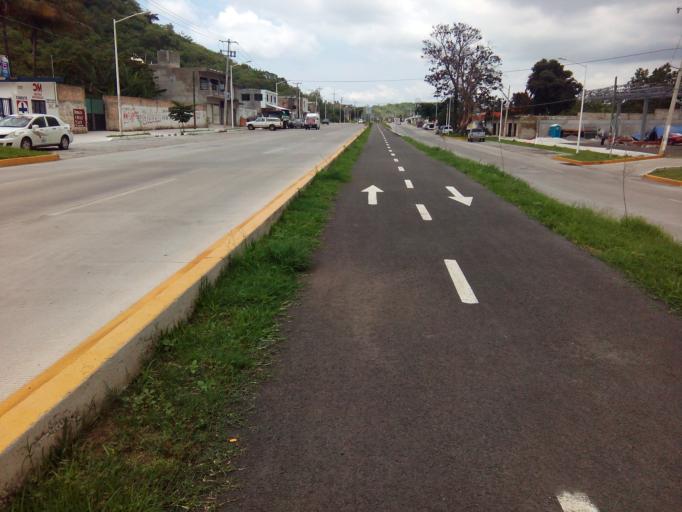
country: MX
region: Nayarit
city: Tepic
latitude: 21.5391
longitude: -104.8686
